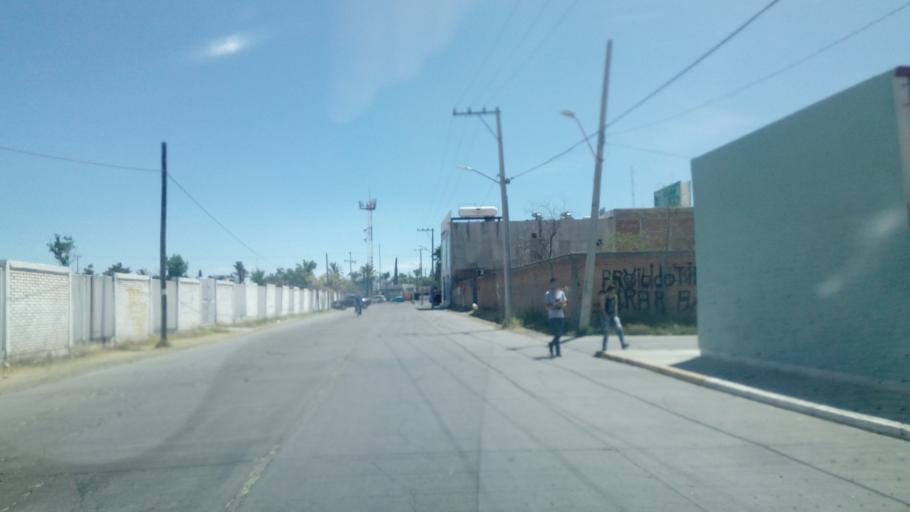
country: MX
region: Durango
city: Victoria de Durango
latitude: 24.0097
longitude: -104.6597
